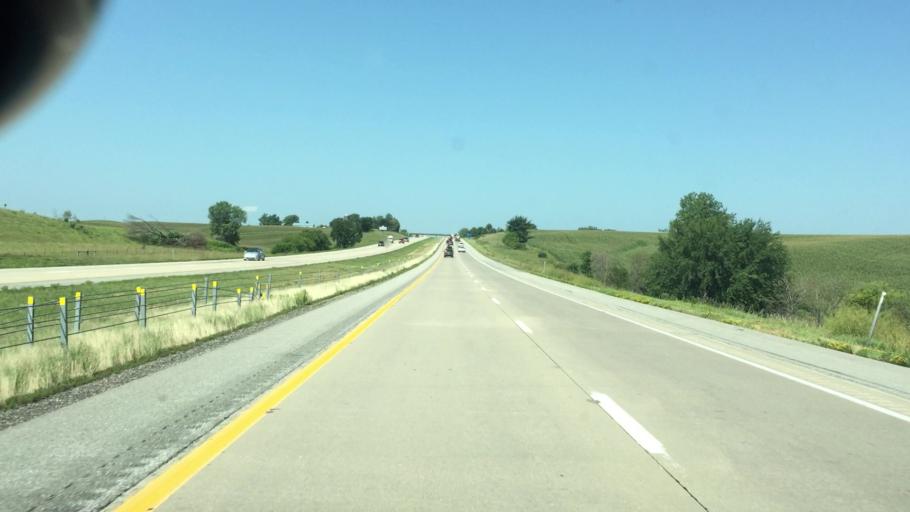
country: US
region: Iowa
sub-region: Poweshiek County
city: Brooklyn
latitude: 41.6961
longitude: -92.3843
